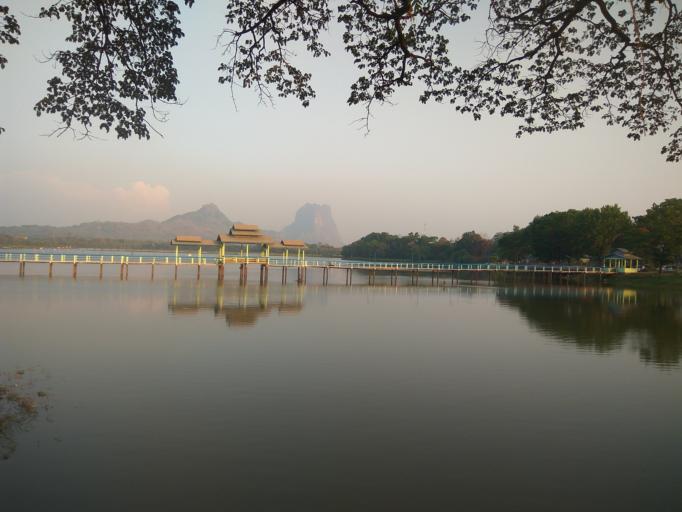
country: MM
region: Kayin
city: Hpa-an
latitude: 16.8832
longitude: 97.6307
